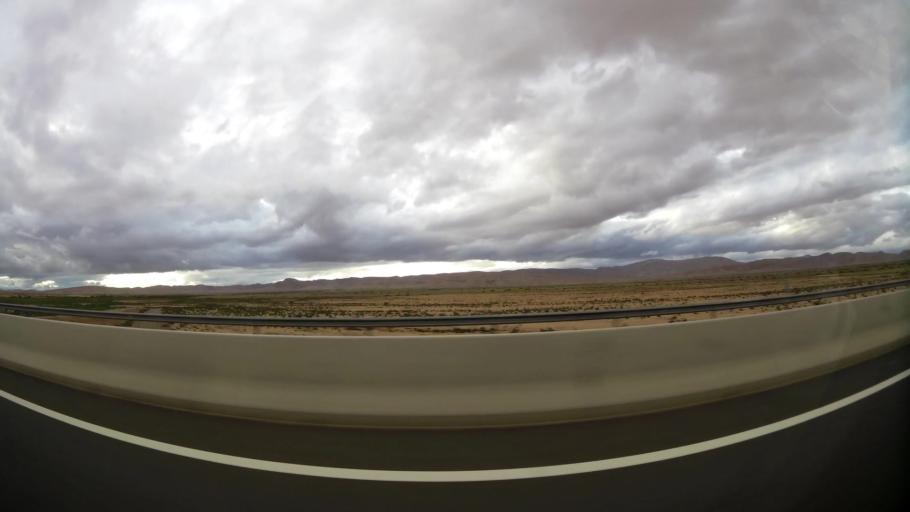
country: MA
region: Taza-Al Hoceima-Taounate
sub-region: Taza
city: Guercif
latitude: 34.3073
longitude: -3.6158
